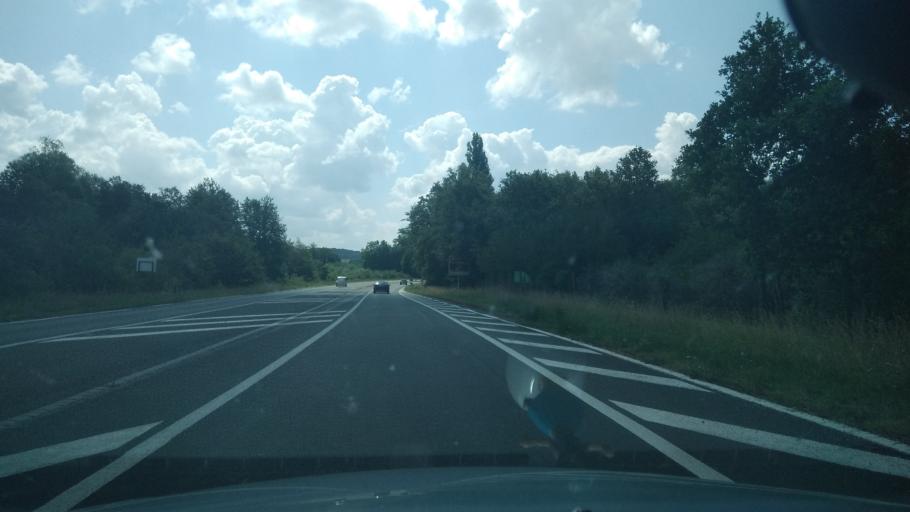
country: FR
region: Poitou-Charentes
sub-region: Departement de la Vienne
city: Les Ormes
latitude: 46.9960
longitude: 0.5954
